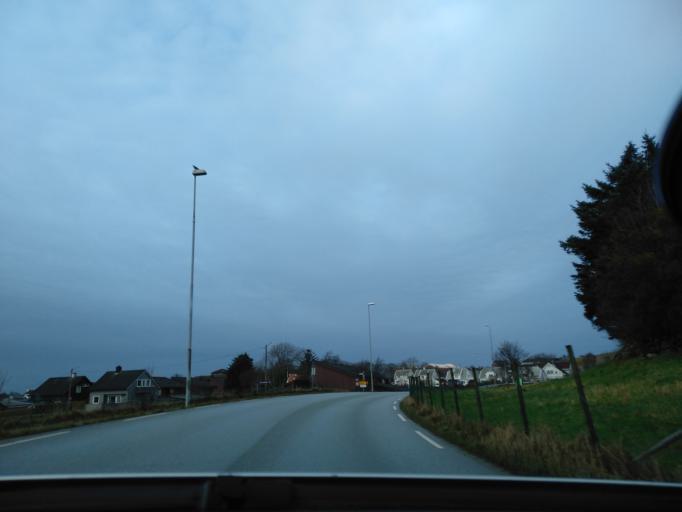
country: NO
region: Rogaland
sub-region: Randaberg
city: Randaberg
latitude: 58.9974
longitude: 5.6265
